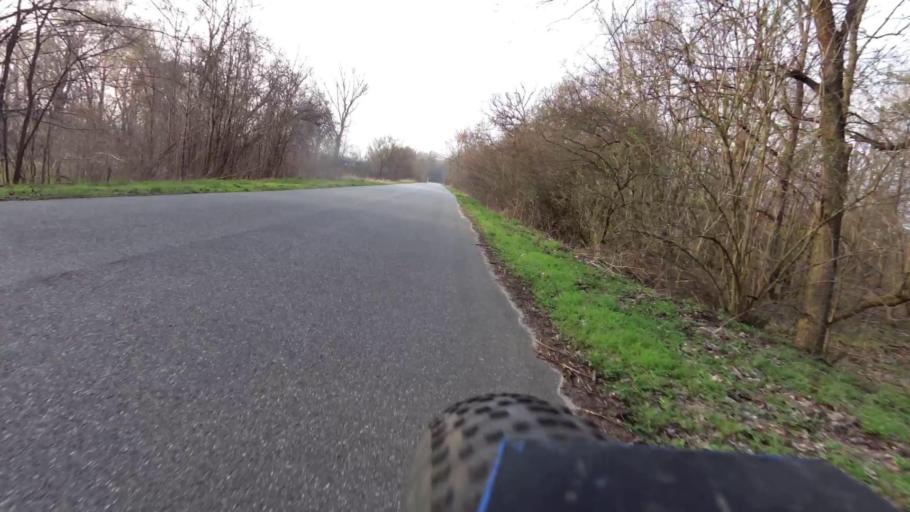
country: DE
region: Brandenburg
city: Vogelsang
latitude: 52.2478
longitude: 14.7064
